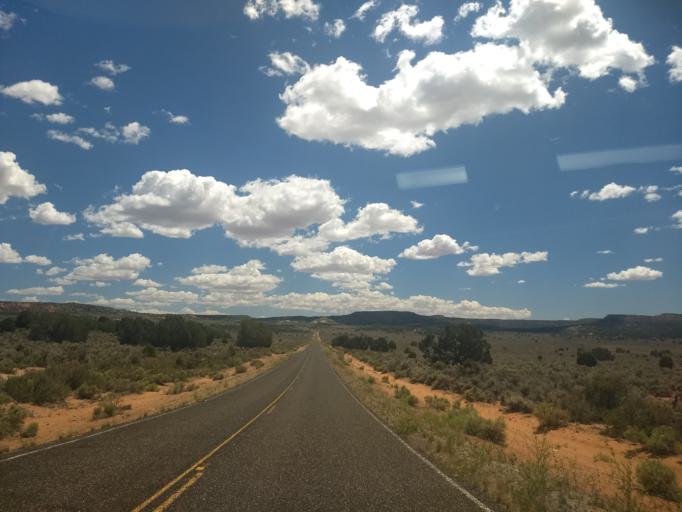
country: US
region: Utah
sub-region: Kane County
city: Kanab
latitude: 37.1705
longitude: -112.6623
